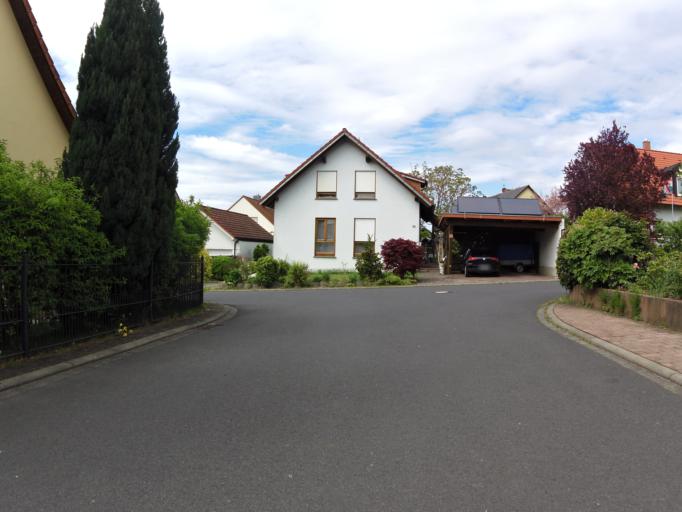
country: DE
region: Bavaria
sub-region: Regierungsbezirk Unterfranken
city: Kurnach
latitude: 49.8429
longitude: 10.0436
